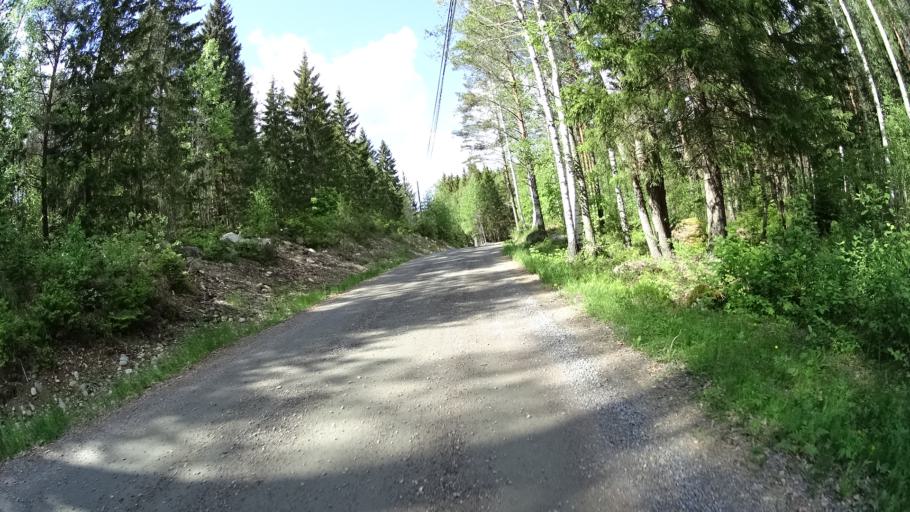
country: FI
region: Uusimaa
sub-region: Raaseporin
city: Pohja
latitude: 60.1722
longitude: 23.5877
